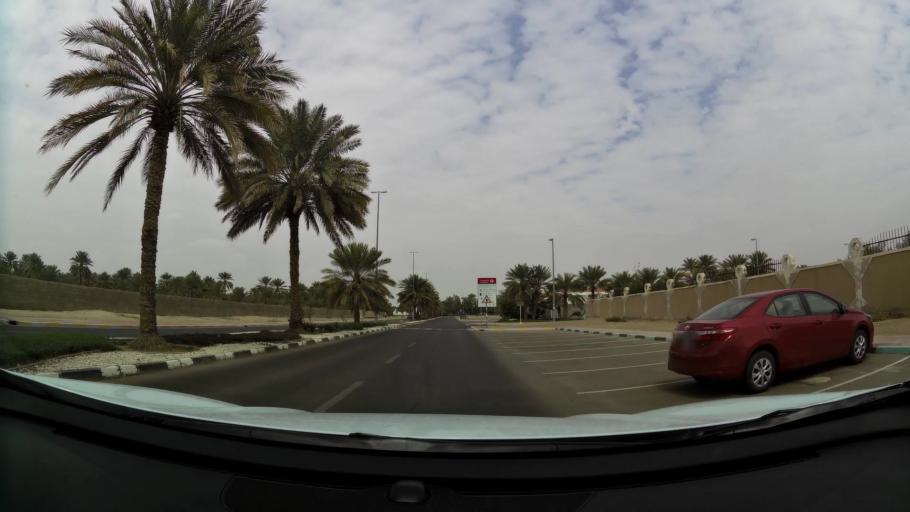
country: OM
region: Al Buraimi
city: Al Buraymi
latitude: 24.2268
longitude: 55.7798
